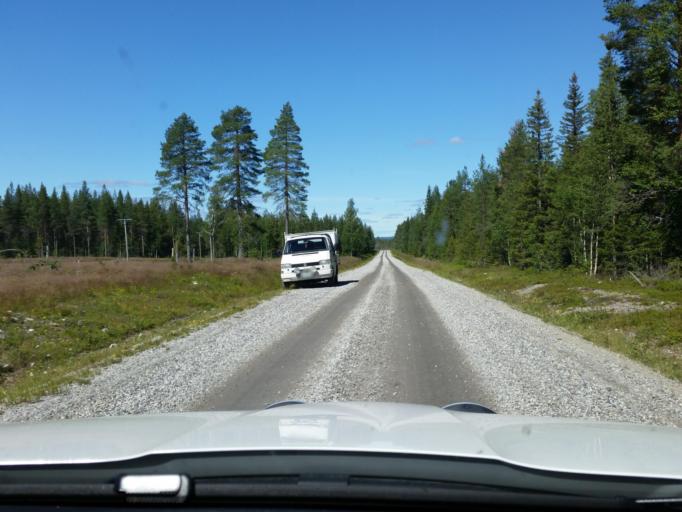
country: SE
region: Vaesterbotten
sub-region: Skelleftea Kommun
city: Storvik
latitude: 65.2648
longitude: 20.6857
